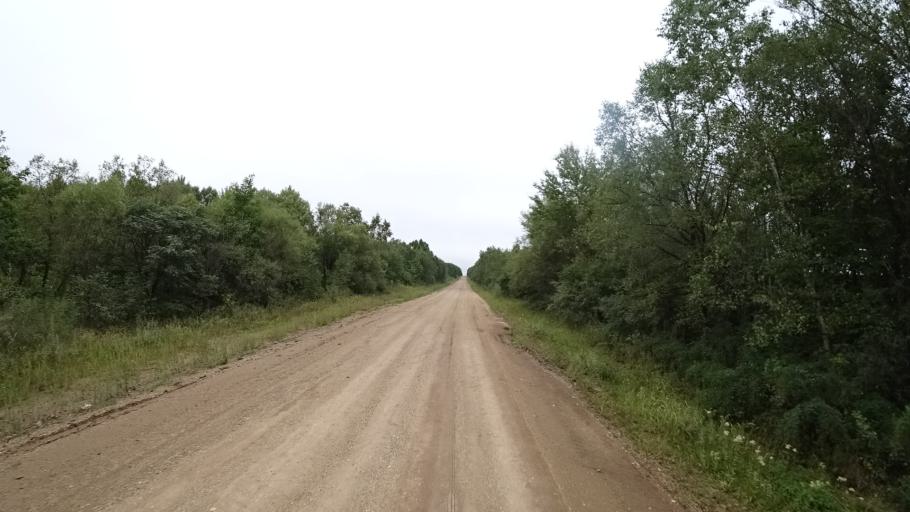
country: RU
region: Primorskiy
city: Ivanovka
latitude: 44.0253
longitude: 132.5245
